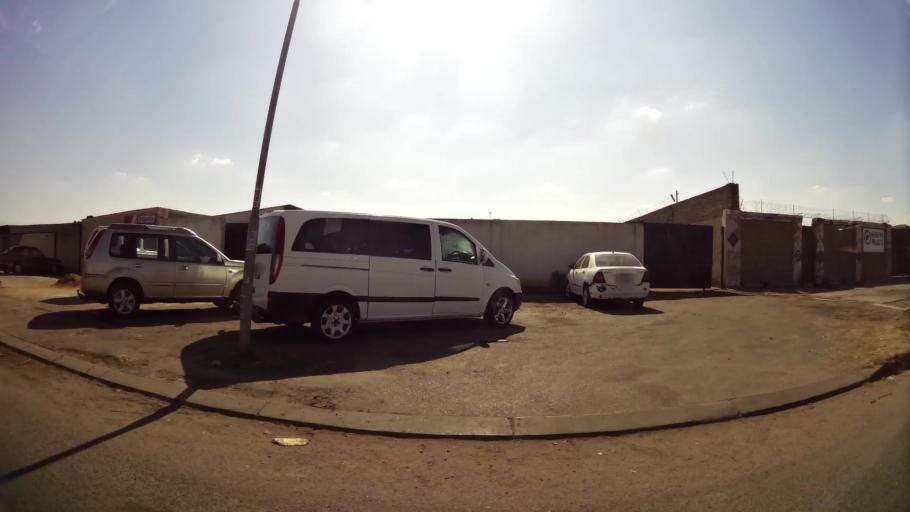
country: ZA
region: Gauteng
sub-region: City of Johannesburg Metropolitan Municipality
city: Soweto
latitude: -26.2922
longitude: 27.8529
